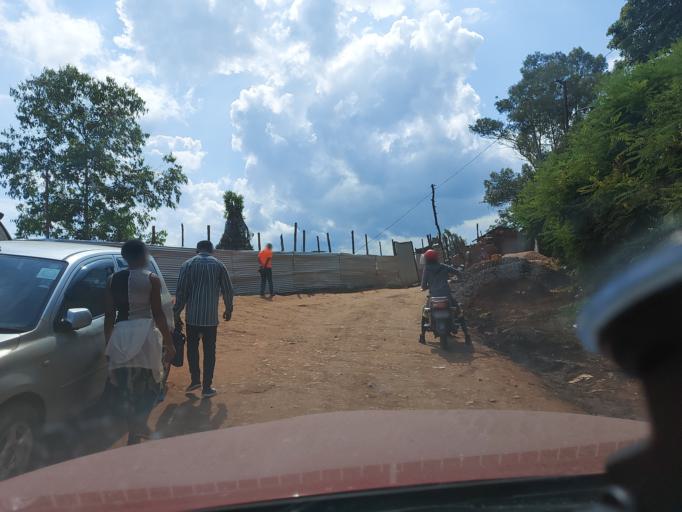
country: CD
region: South Kivu
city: Bukavu
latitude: -2.4946
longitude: 28.8587
